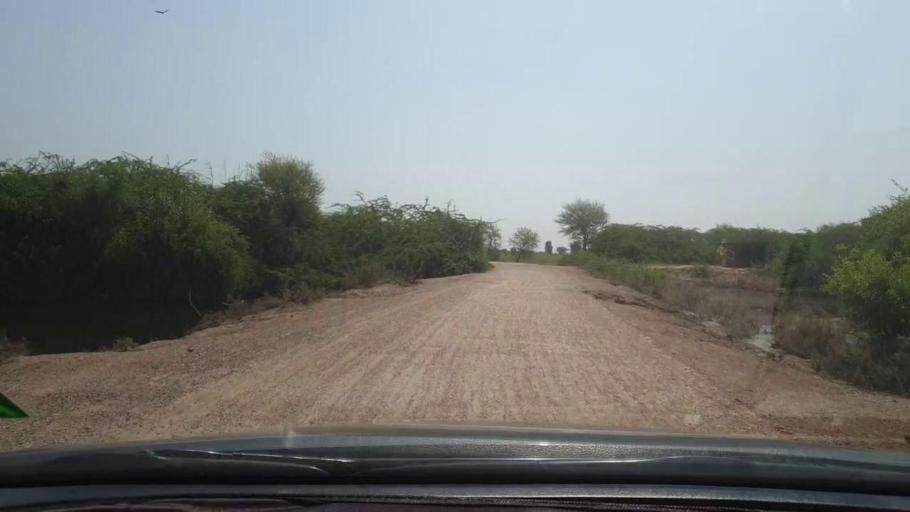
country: PK
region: Sindh
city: Tando Bago
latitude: 24.7851
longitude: 69.1748
